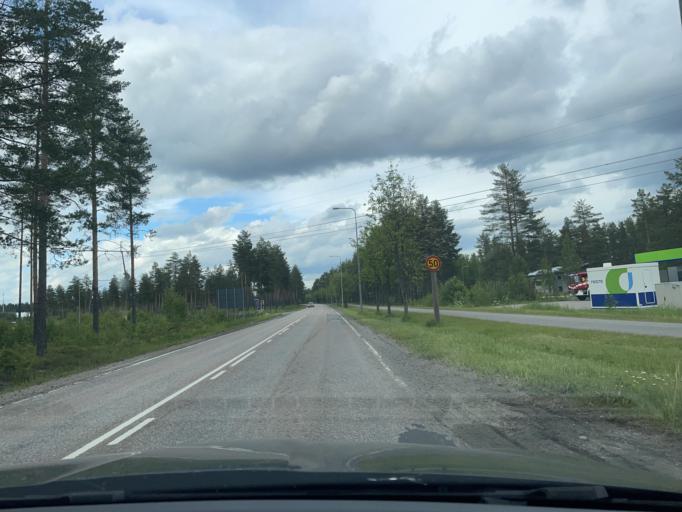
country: FI
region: Central Finland
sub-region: Jaemsae
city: Jaemsaenkoski
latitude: 61.9103
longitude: 25.1406
